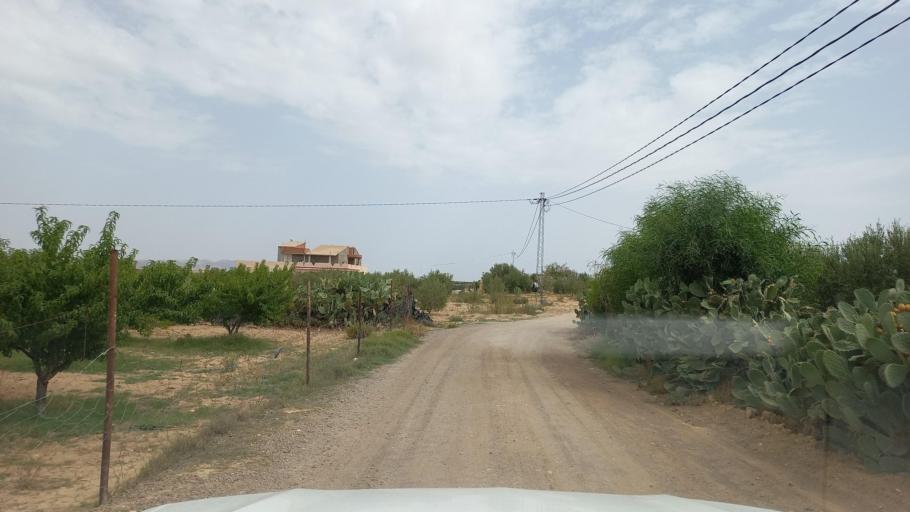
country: TN
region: Al Qasrayn
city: Kasserine
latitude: 35.2683
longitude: 9.0026
